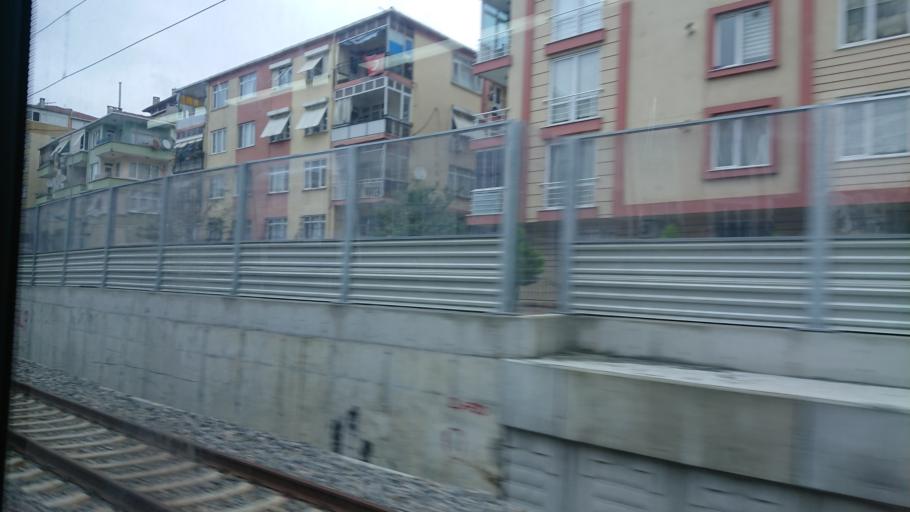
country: TR
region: Istanbul
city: Mahmutbey
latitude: 40.9976
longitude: 28.7675
